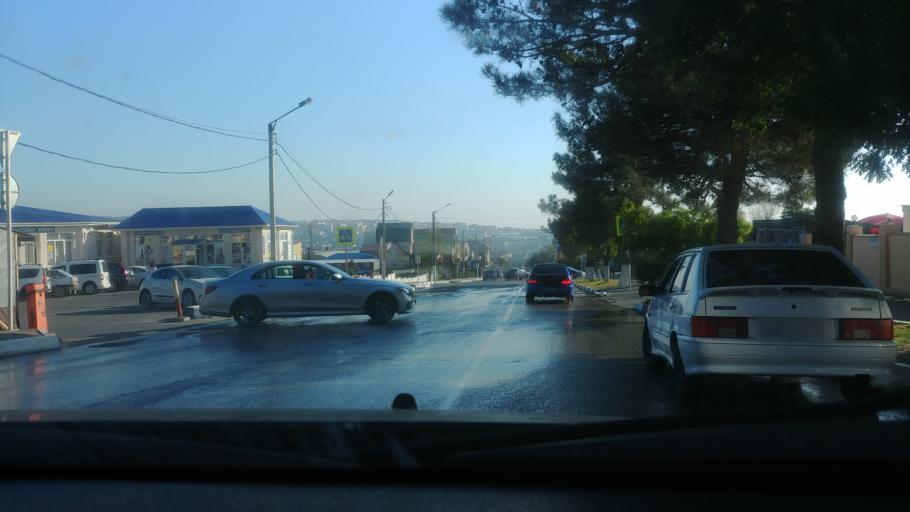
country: RU
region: Krasnodarskiy
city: Gelendzhik
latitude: 44.5707
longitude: 38.0922
